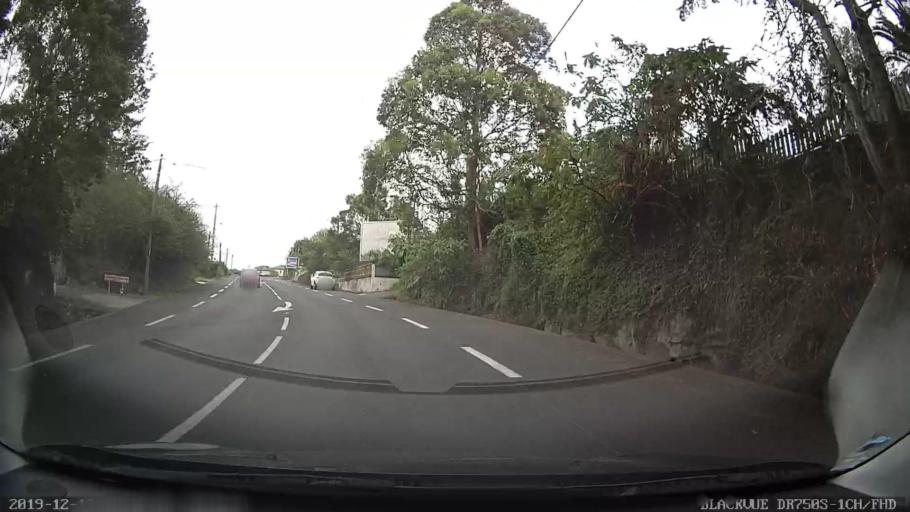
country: RE
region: Reunion
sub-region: Reunion
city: Le Tampon
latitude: -21.2474
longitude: 55.5264
